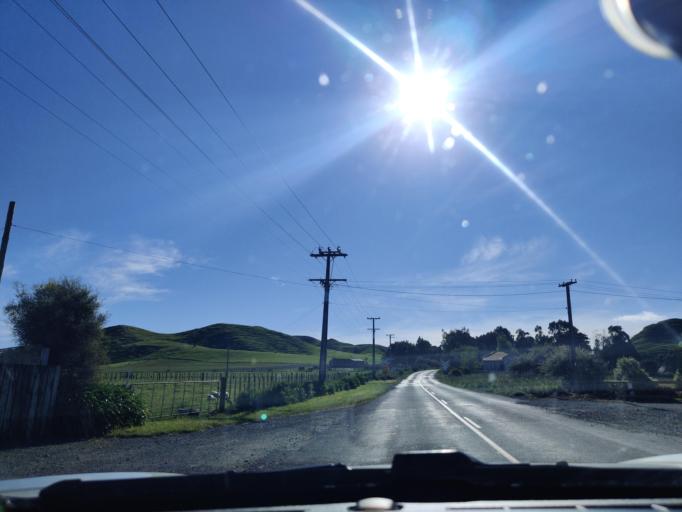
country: NZ
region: Manawatu-Wanganui
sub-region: Palmerston North City
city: Palmerston North
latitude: -40.5152
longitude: 175.7480
